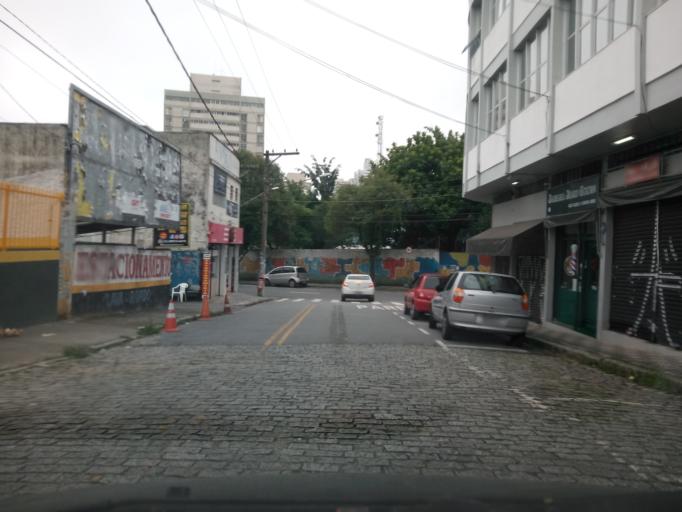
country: BR
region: Sao Paulo
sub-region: Sao Bernardo Do Campo
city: Sao Bernardo do Campo
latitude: -23.7166
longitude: -46.5484
